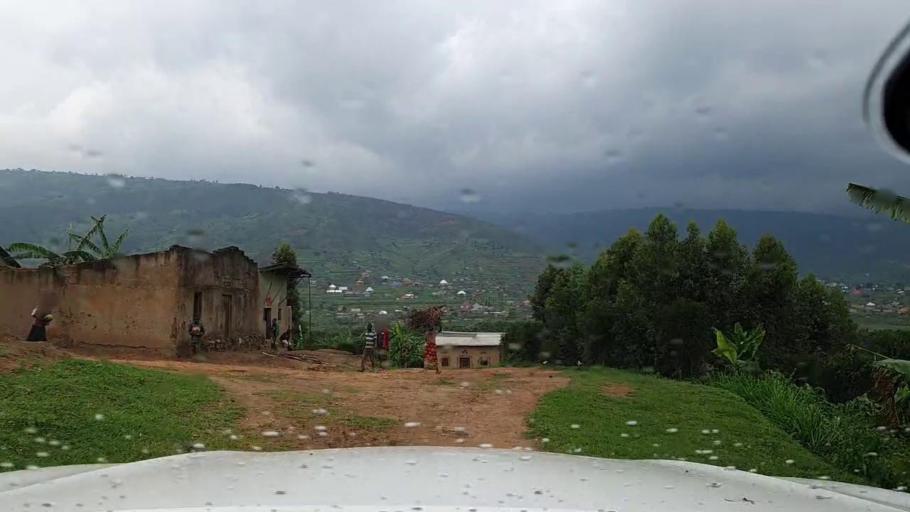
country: RW
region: Kigali
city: Kigali
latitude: -1.8979
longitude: 29.9533
